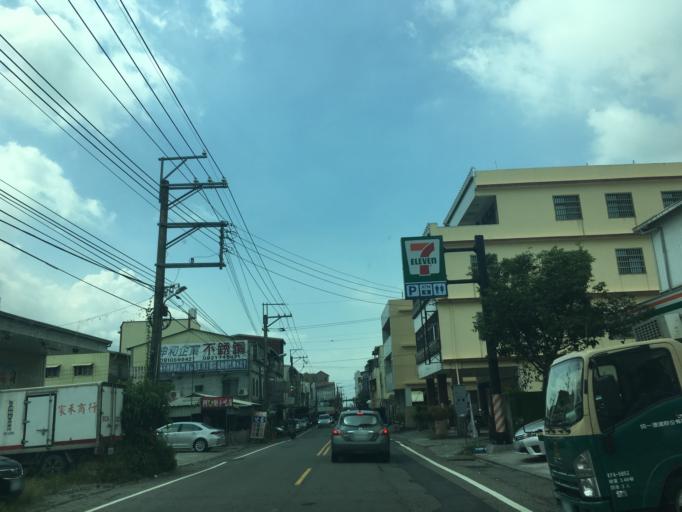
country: TW
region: Taiwan
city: Fengyuan
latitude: 24.2170
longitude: 120.7960
